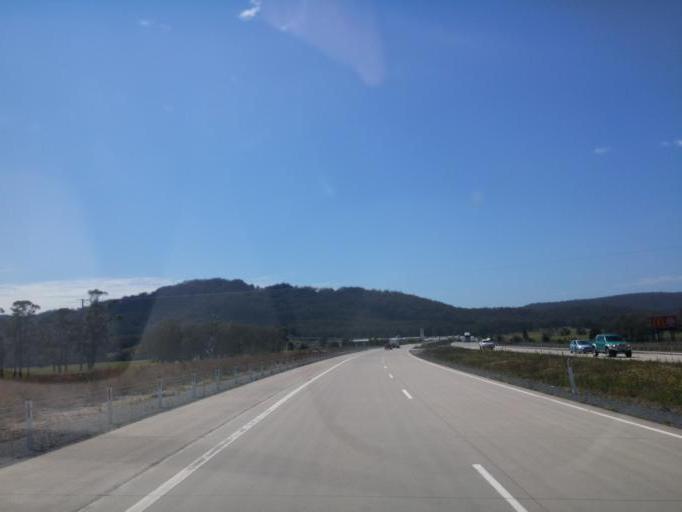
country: AU
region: New South Wales
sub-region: Great Lakes
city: Bulahdelah
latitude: -32.4239
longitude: 152.2009
